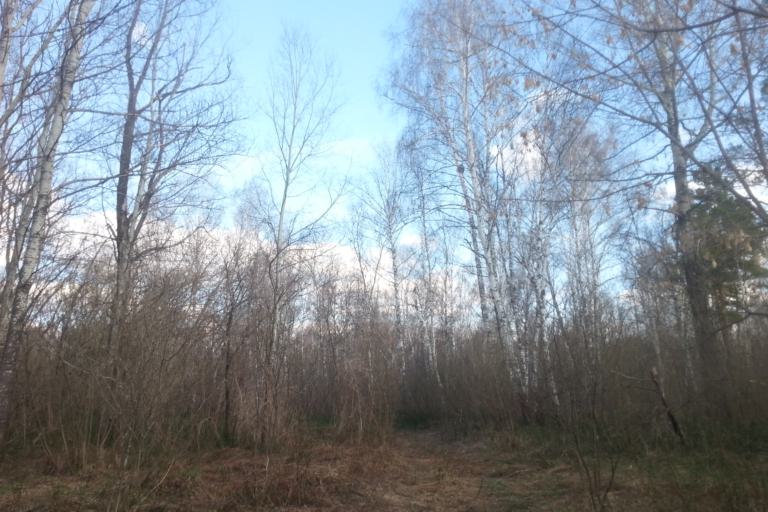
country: RU
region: Altai Krai
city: Sannikovo
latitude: 53.3311
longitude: 84.0216
